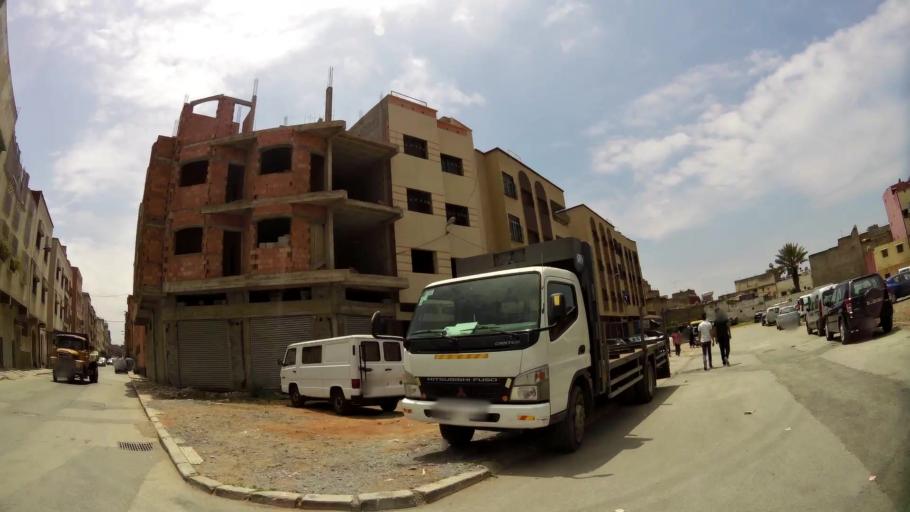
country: MA
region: Rabat-Sale-Zemmour-Zaer
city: Sale
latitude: 34.0542
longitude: -6.7874
